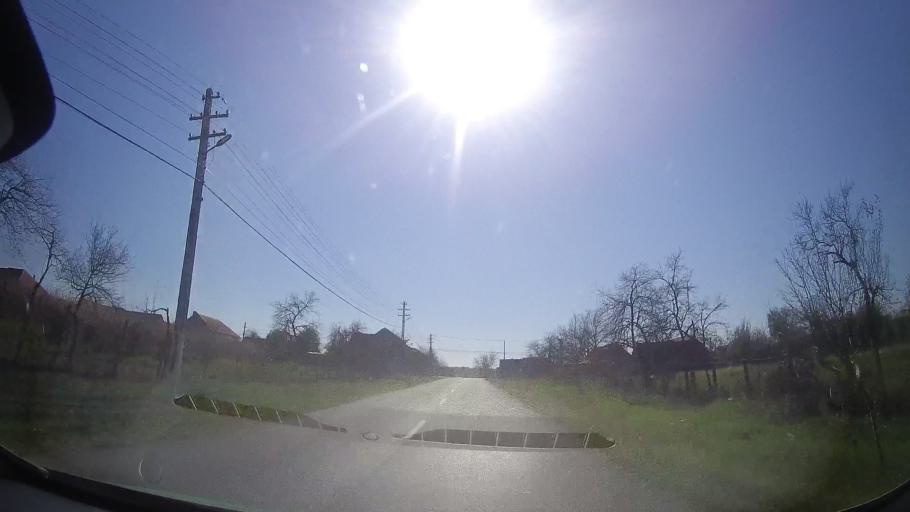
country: RO
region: Timis
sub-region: Comuna Bethausen
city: Bethausen
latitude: 45.7947
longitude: 21.9646
